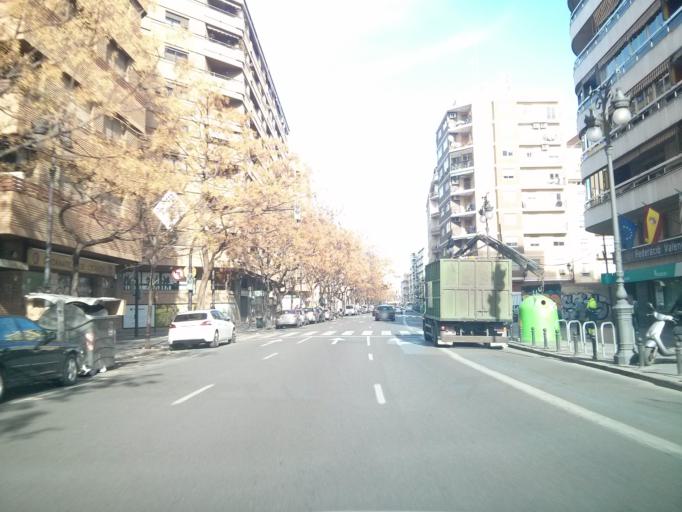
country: ES
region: Valencia
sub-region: Provincia de Valencia
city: Valencia
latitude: 39.4718
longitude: -0.3840
